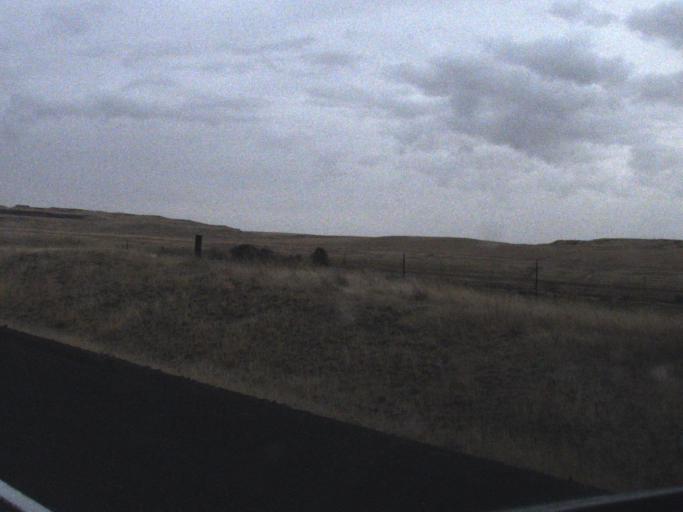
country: US
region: Washington
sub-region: Adams County
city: Ritzville
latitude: 46.7681
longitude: -118.1297
